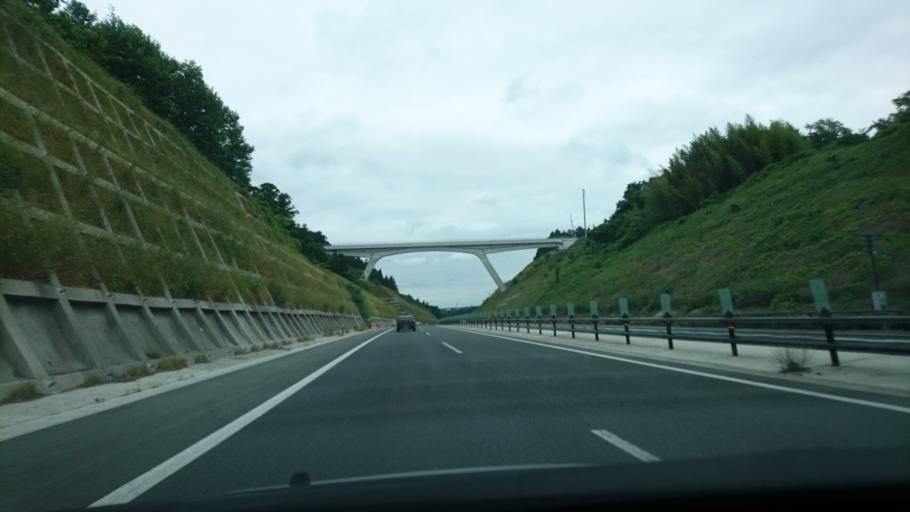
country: JP
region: Miyagi
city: Ishinomaki
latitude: 38.5422
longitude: 141.2745
